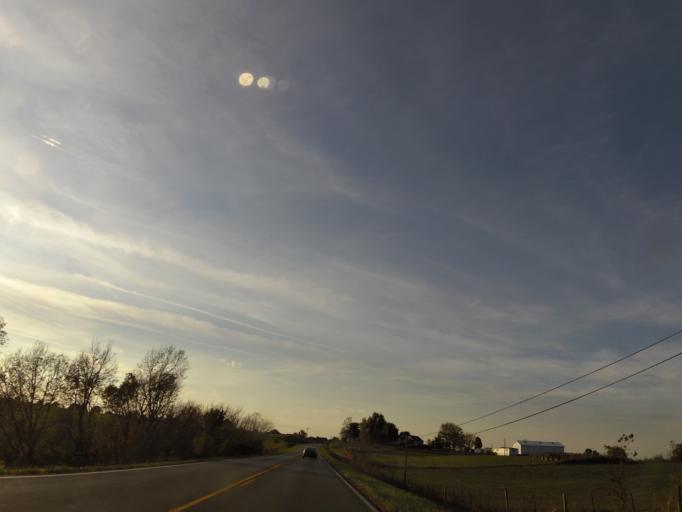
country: US
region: Kentucky
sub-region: Garrard County
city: Lancaster
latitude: 37.6519
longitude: -84.6007
